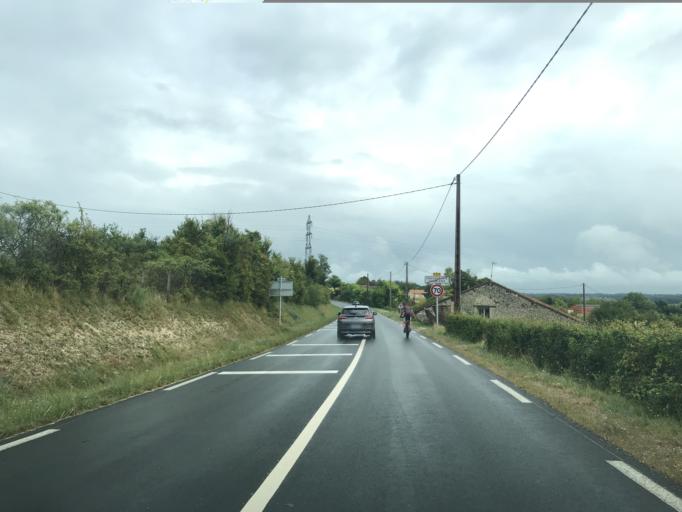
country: FR
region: Aquitaine
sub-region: Departement de la Dordogne
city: Coulounieix-Chamiers
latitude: 45.1569
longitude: 0.6990
